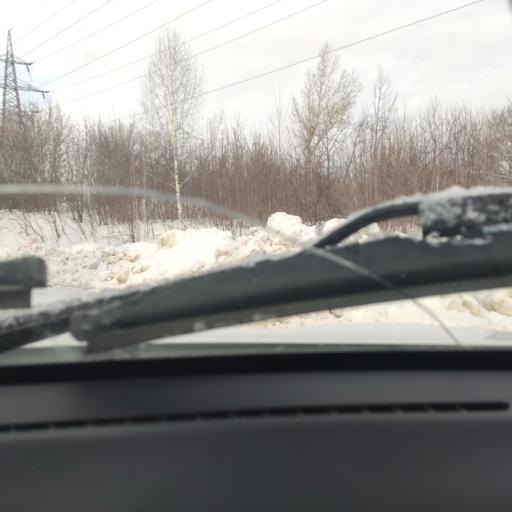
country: RU
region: Tatarstan
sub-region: Gorod Kazan'
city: Kazan
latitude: 55.8432
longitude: 49.0721
